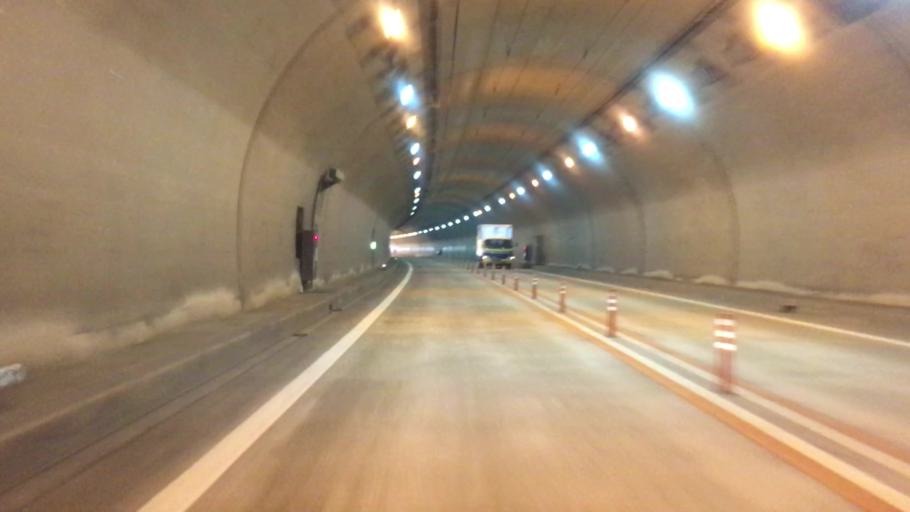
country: JP
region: Tottori
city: Tottori
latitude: 35.4098
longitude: 134.2072
